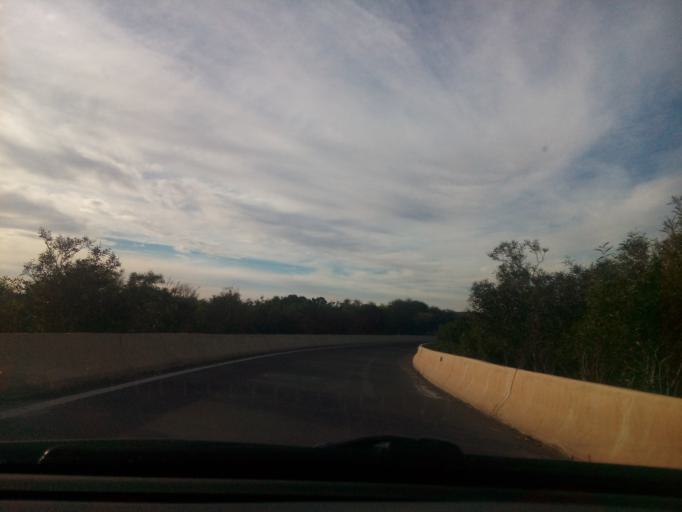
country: DZ
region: Mascara
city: Mascara
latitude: 35.6247
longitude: 0.0742
